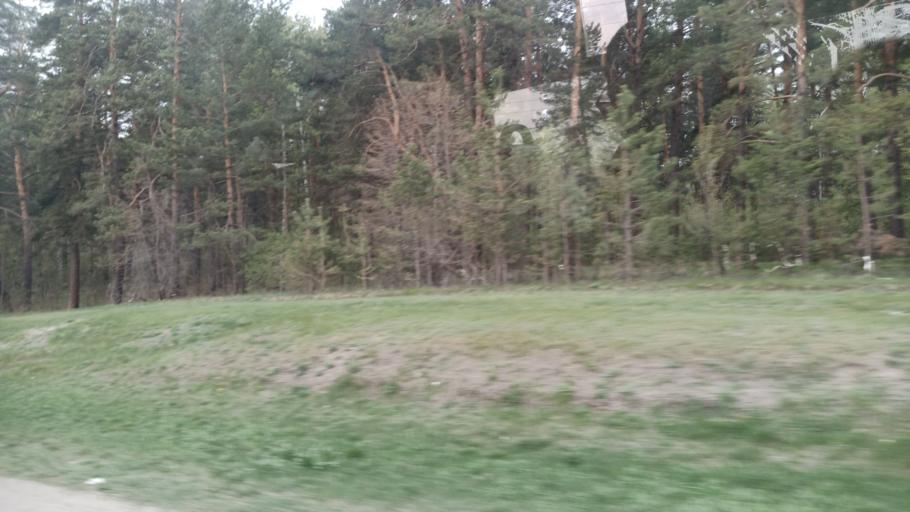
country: RU
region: Altai Krai
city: Yuzhnyy
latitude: 53.2645
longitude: 83.7084
